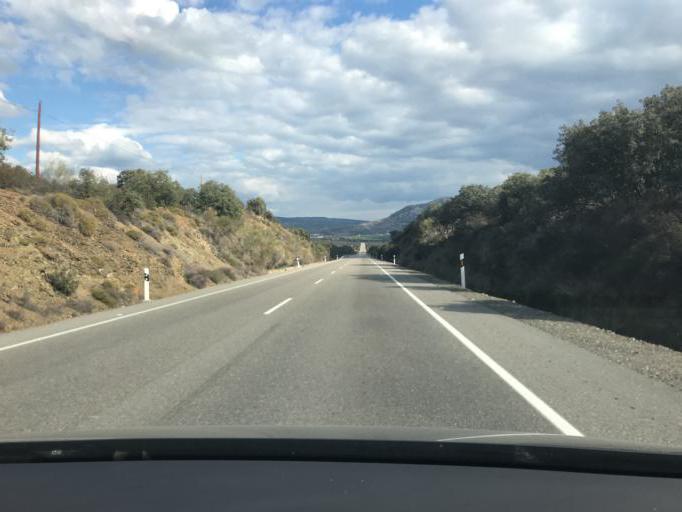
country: ES
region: Andalusia
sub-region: Province of Cordoba
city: Espiel
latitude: 38.1900
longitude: -5.0882
